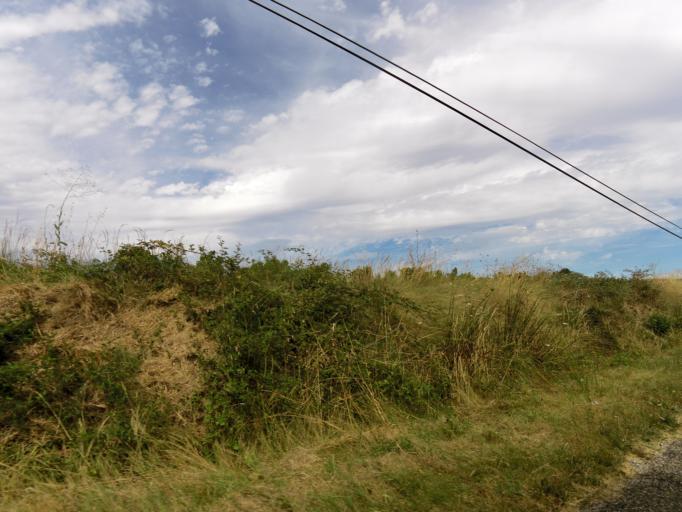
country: FR
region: Languedoc-Roussillon
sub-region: Departement du Gard
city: Villevieille
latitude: 43.8217
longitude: 4.1377
